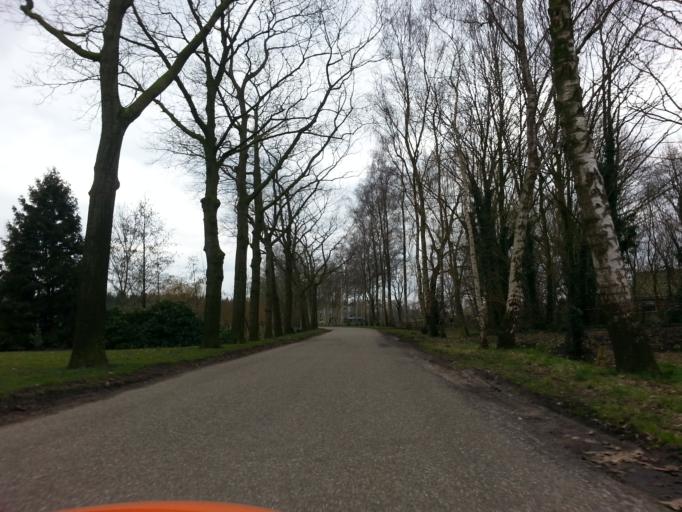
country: NL
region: Gelderland
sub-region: Gemeente Barneveld
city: Terschuur
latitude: 52.1048
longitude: 5.4996
